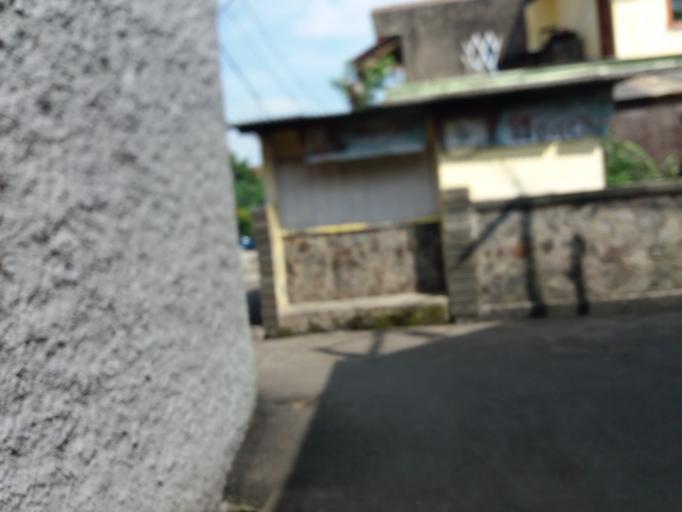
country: ID
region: West Java
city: Bandung
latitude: -6.9186
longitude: 107.6552
